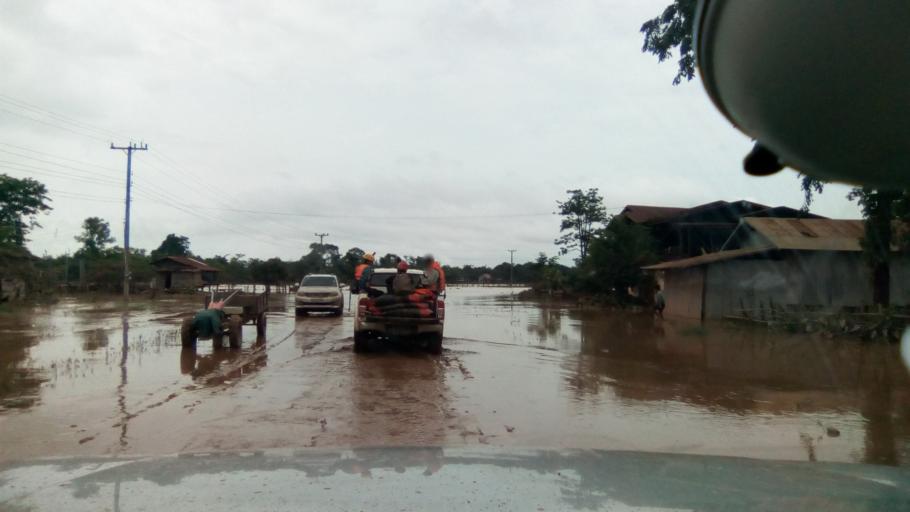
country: LA
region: Attapu
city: Attapu
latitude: 14.7009
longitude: 106.5299
